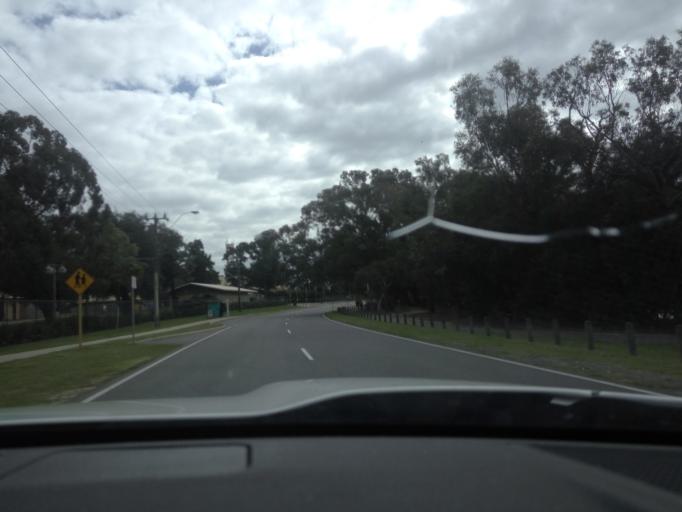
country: AU
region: Western Australia
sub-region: City of Cockburn
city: Bibra Lake
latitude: -32.0973
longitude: 115.8200
